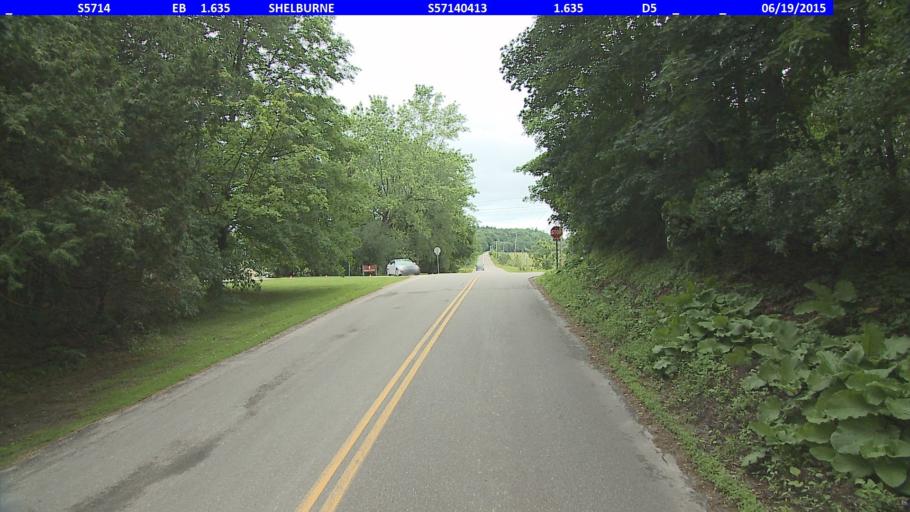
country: US
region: Vermont
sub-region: Chittenden County
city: Burlington
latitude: 44.3951
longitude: -73.2466
